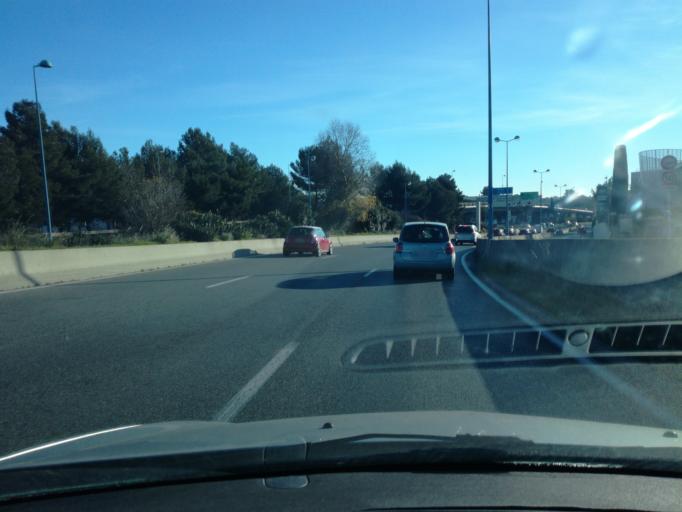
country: FR
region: Provence-Alpes-Cote d'Azur
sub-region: Departement des Alpes-Maritimes
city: Biot
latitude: 43.6022
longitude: 7.0817
